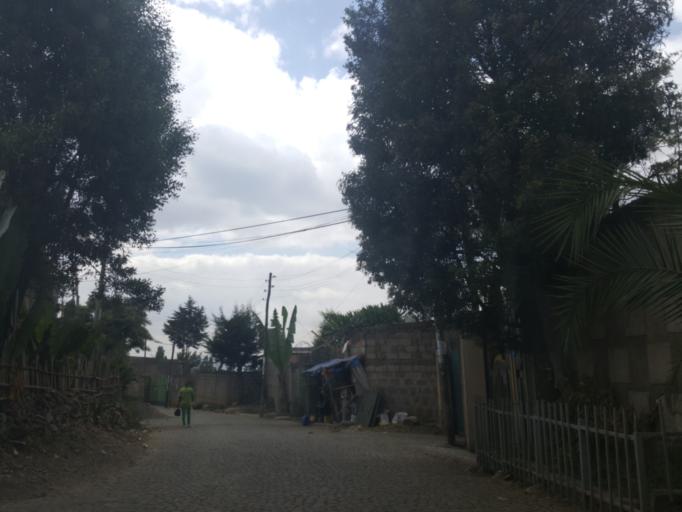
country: ET
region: Adis Abeba
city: Addis Ababa
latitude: 9.0610
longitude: 38.7184
